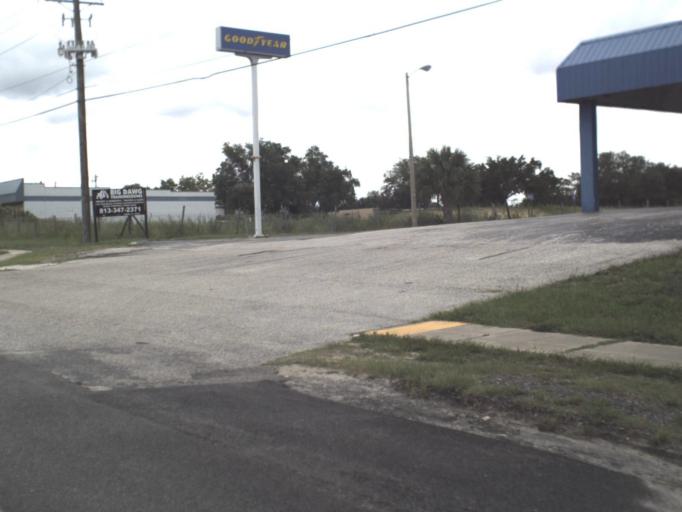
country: US
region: Florida
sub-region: Hillsborough County
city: East Lake-Orient Park
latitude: 27.9963
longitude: -82.3857
